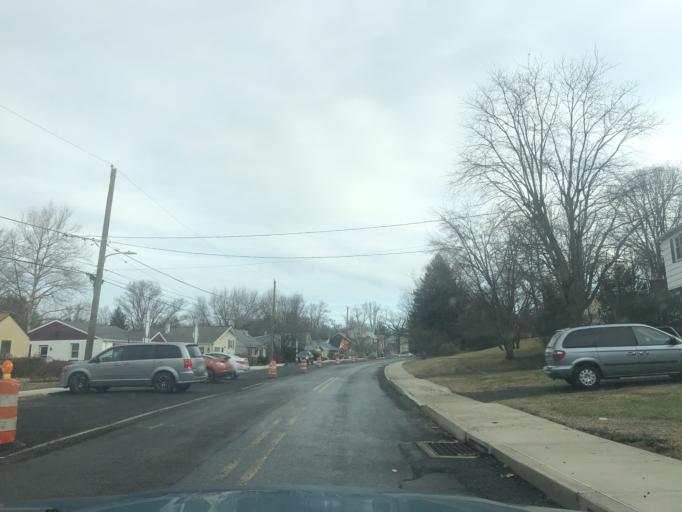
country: US
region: Pennsylvania
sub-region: Montgomery County
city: Glenside
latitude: 40.1156
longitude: -75.1508
